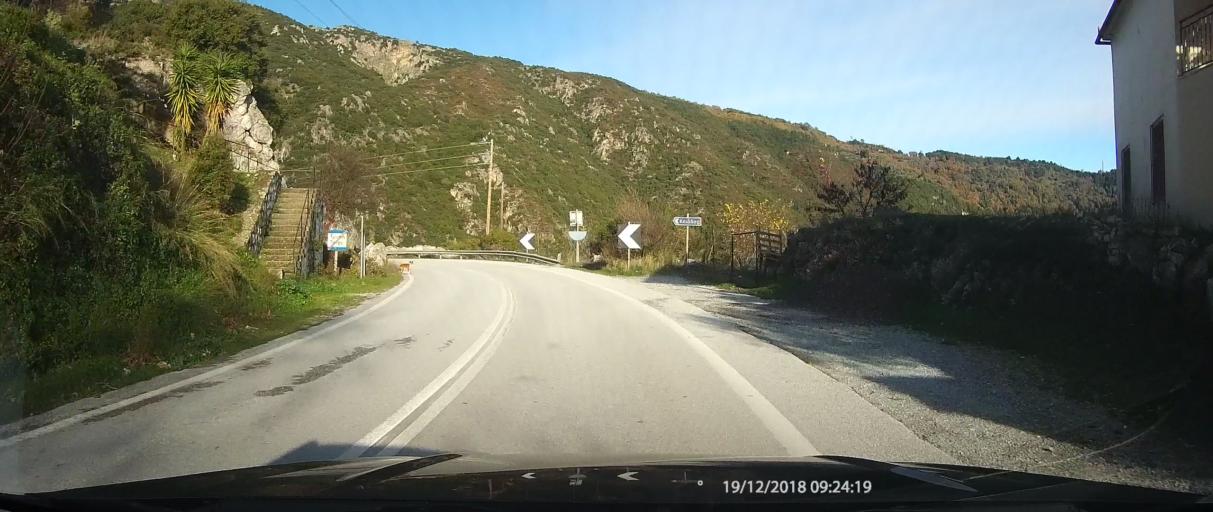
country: GR
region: Peloponnese
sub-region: Nomos Lakonias
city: Magoula
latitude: 37.0957
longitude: 22.3409
